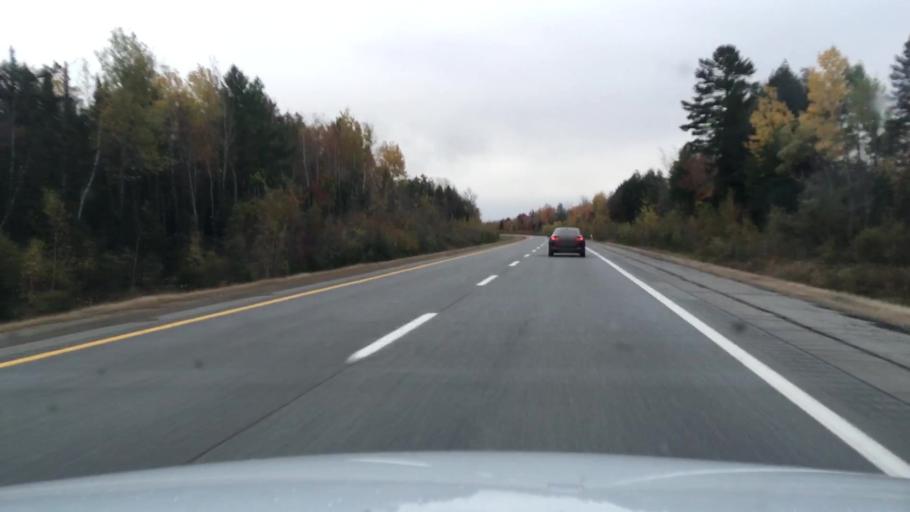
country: US
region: Maine
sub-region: Penobscot County
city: Greenbush
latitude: 45.1008
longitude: -68.6962
